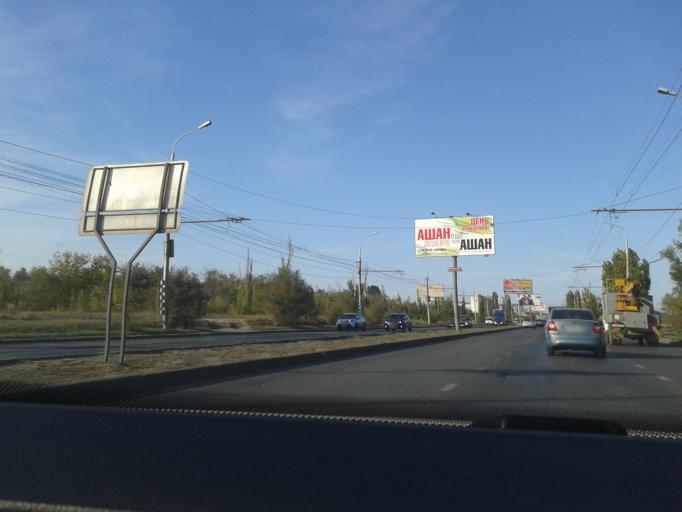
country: RU
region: Volgograd
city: Volgograd
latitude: 48.6299
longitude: 44.4279
